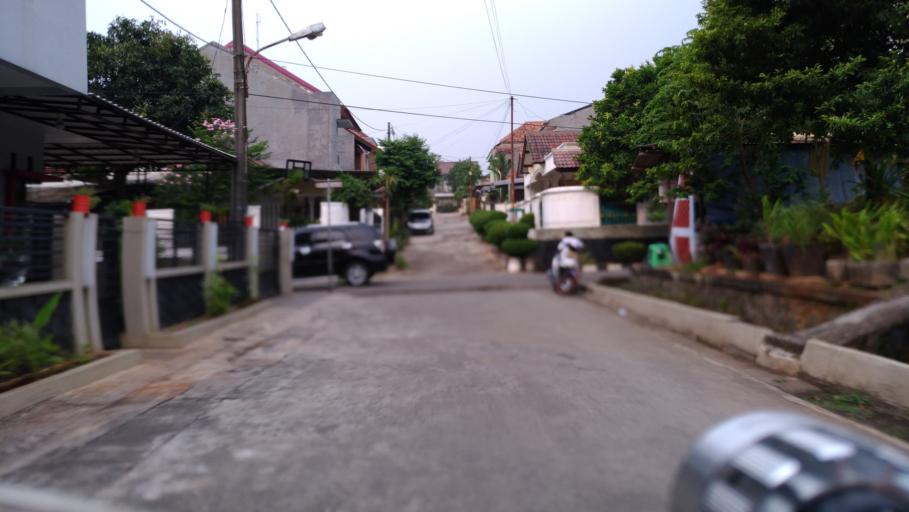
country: ID
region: West Java
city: Depok
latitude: -6.3636
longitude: 106.8645
